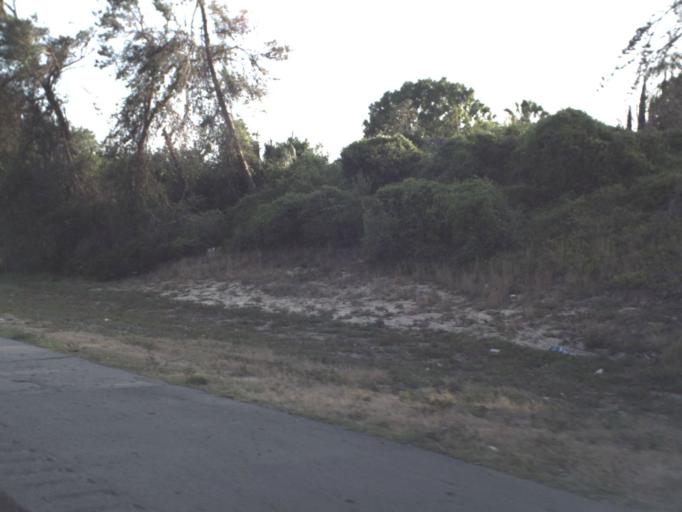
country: US
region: Florida
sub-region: Brevard County
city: Titusville
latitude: 28.6071
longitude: -80.8514
